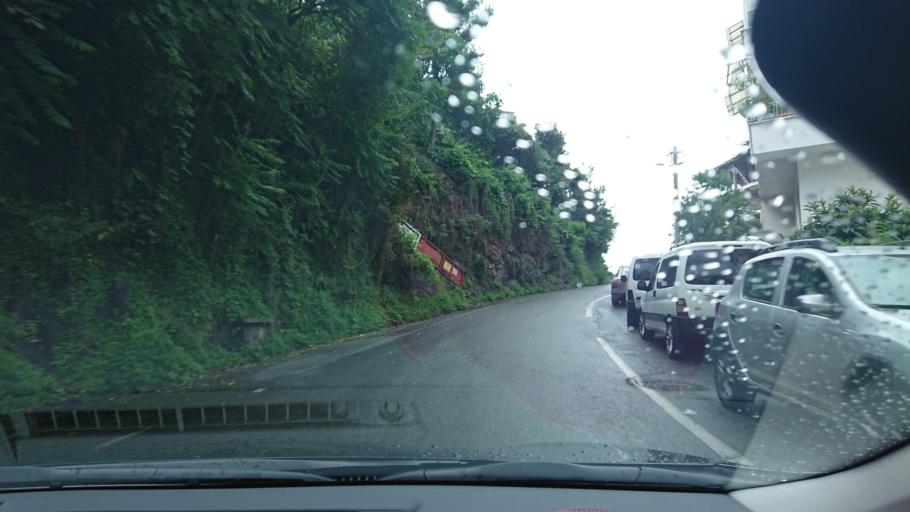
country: TR
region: Rize
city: Rize
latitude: 41.0271
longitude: 40.5114
